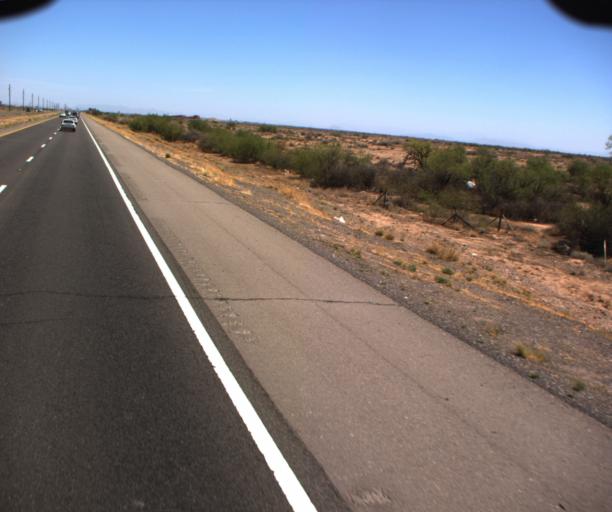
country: US
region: Arizona
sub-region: Maricopa County
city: Sun Lakes
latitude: 33.2372
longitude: -111.9828
